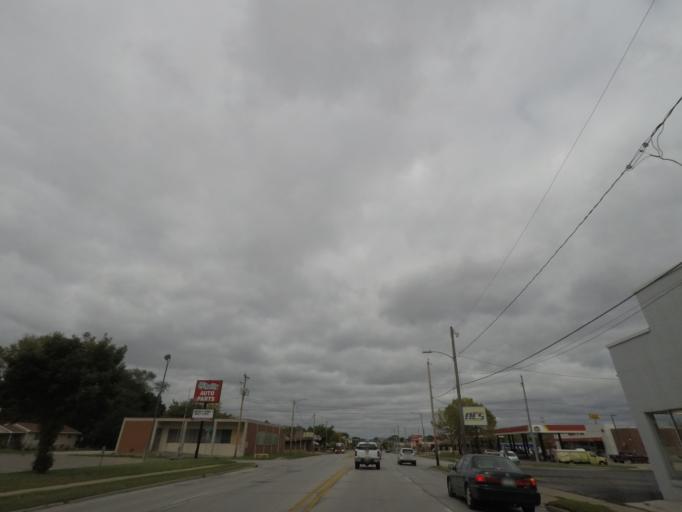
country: US
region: Iowa
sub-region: Polk County
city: Des Moines
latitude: 41.6254
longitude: -93.6005
